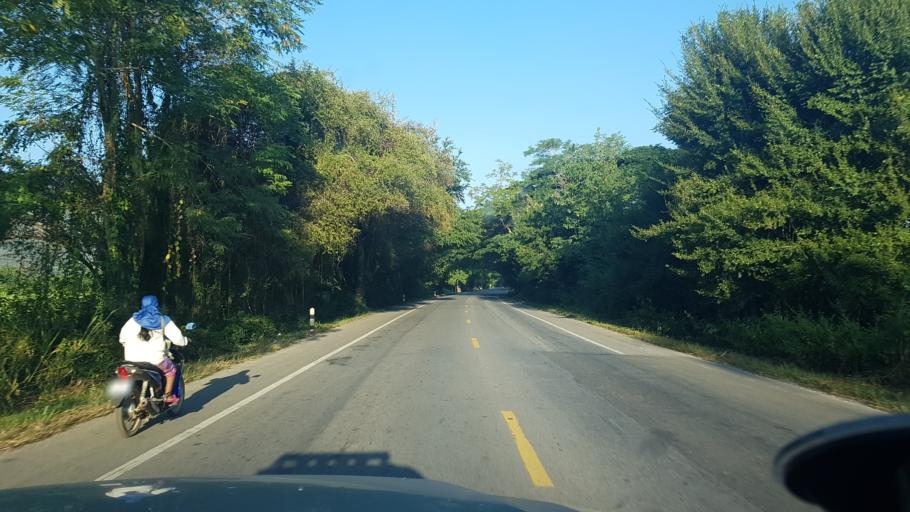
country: TH
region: Chaiyaphum
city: Khon San
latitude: 16.6048
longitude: 101.8908
